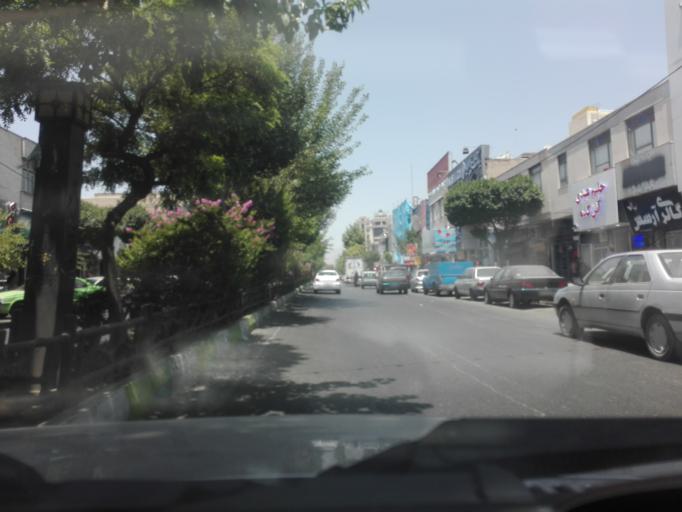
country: IR
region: Tehran
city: Shahre Jadide Andisheh
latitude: 35.7303
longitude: 50.9900
